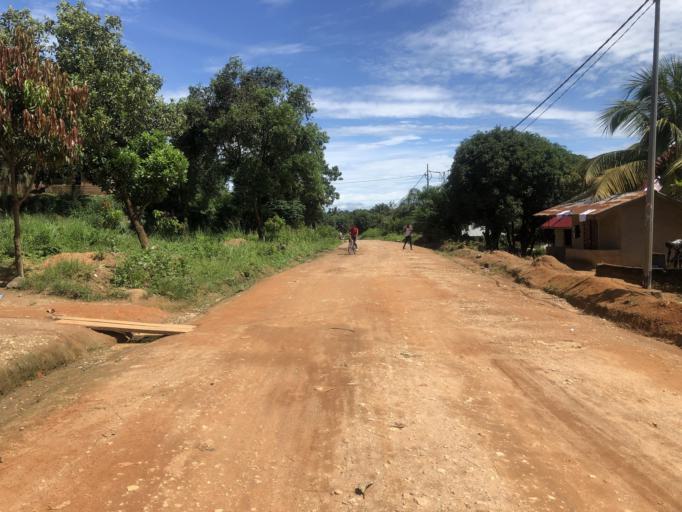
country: SL
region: Eastern Province
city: Koidu
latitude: 8.6418
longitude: -10.9546
